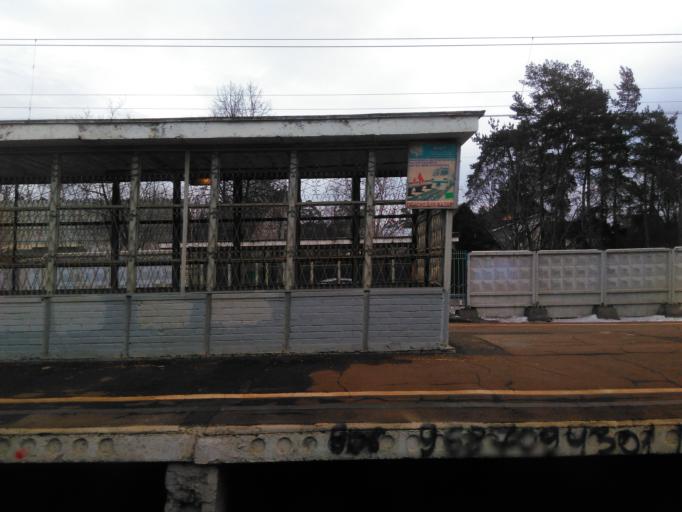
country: RU
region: Moskovskaya
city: Mamontovka
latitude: 55.9786
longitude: 37.8191
